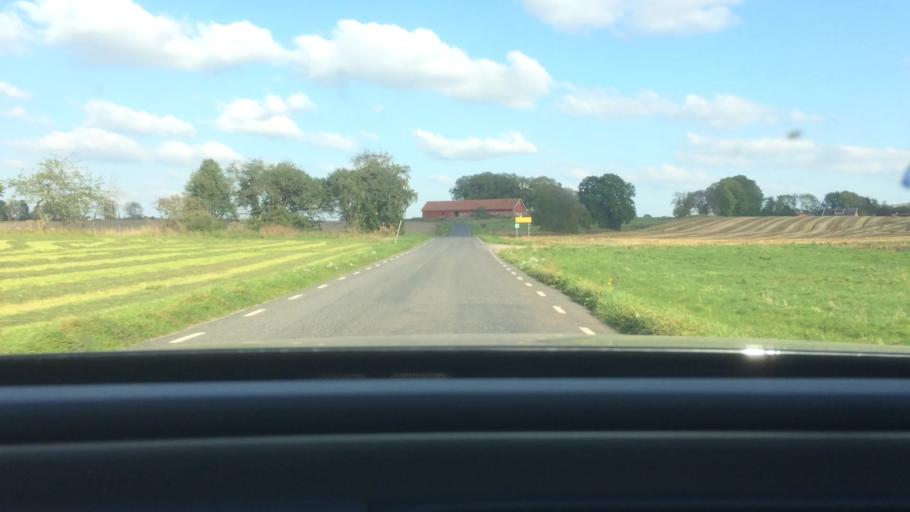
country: SE
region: Vaestra Goetaland
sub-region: Falkopings Kommun
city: Falkoeping
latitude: 58.1406
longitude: 13.5372
